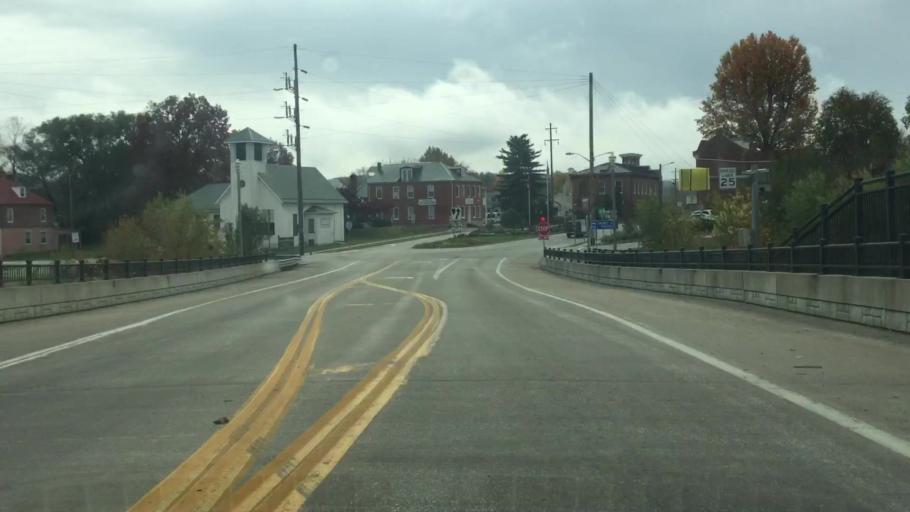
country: US
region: Missouri
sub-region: Gasconade County
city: Hermann
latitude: 38.7077
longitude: -91.4380
